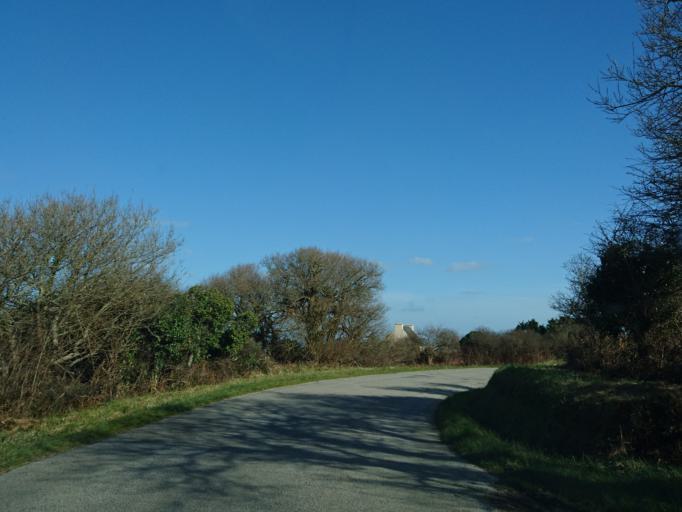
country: FR
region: Brittany
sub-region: Departement du Finistere
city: Roscanvel
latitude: 48.3012
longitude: -4.5638
